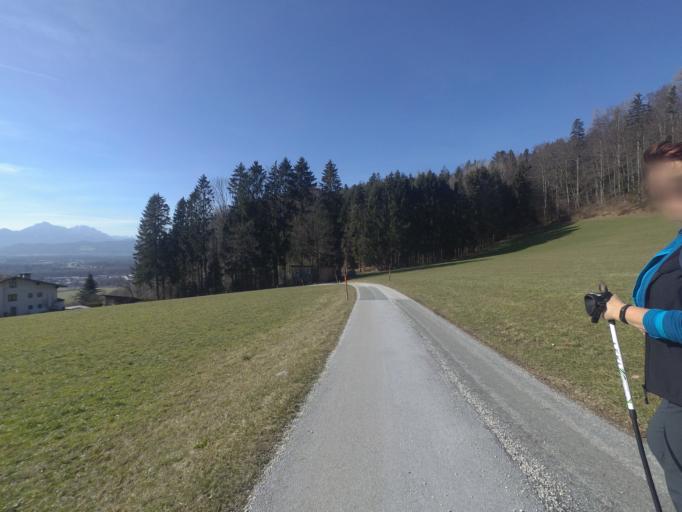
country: AT
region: Salzburg
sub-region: Politischer Bezirk Salzburg-Umgebung
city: Bergheim
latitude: 47.8520
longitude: 13.0353
